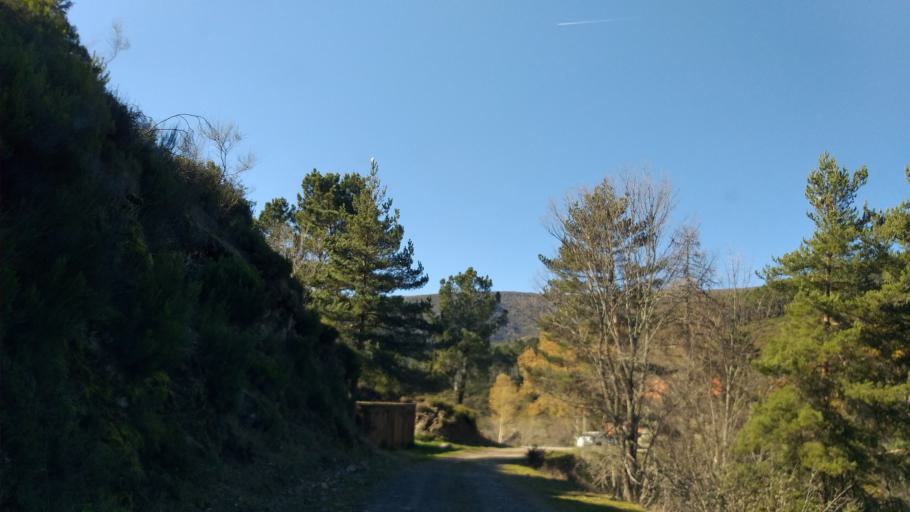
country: PT
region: Guarda
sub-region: Manteigas
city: Manteigas
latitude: 40.4418
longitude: -7.5145
